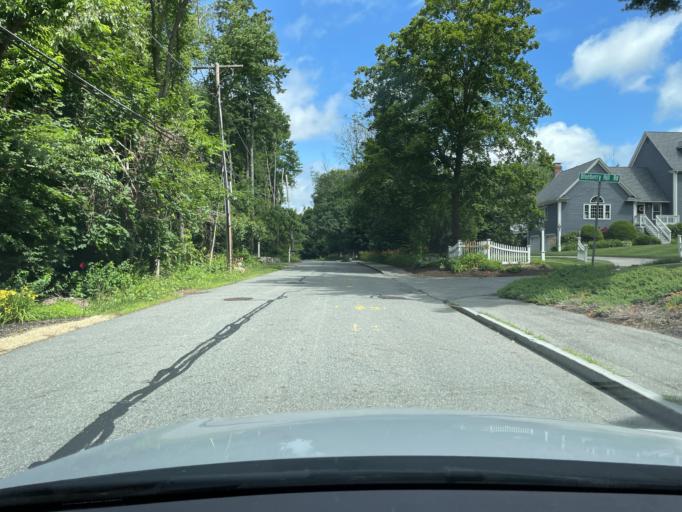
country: US
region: Massachusetts
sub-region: Essex County
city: Andover
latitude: 42.6357
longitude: -71.1219
